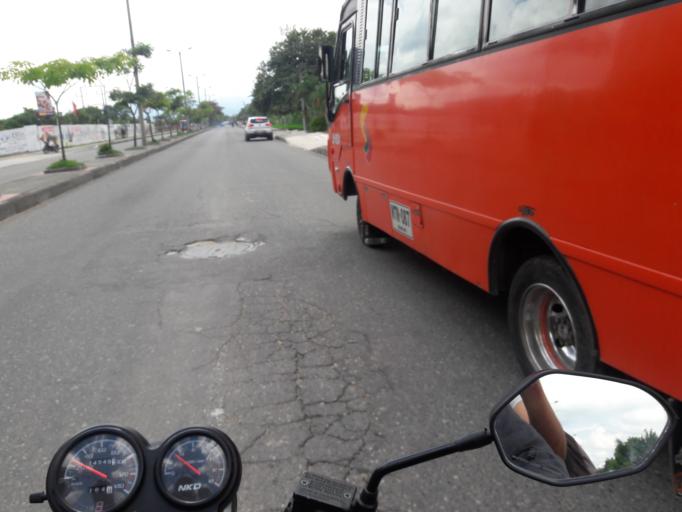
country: CO
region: Tolima
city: Ibague
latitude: 4.4461
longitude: -75.1606
